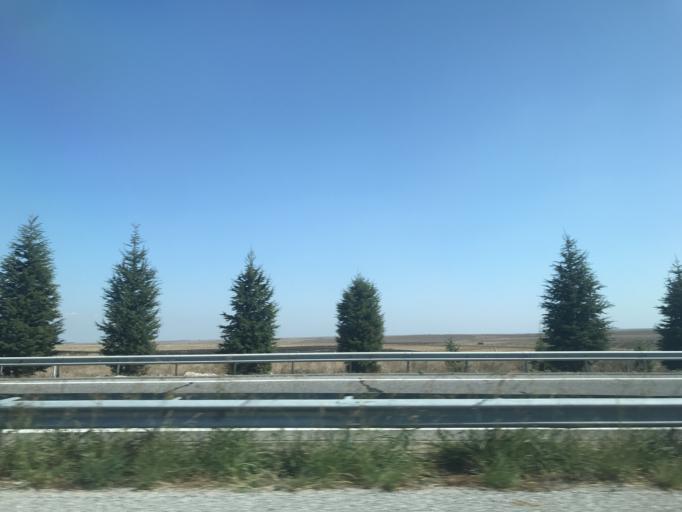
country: TR
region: Kirklareli
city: Luleburgaz
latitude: 41.4000
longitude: 27.3889
